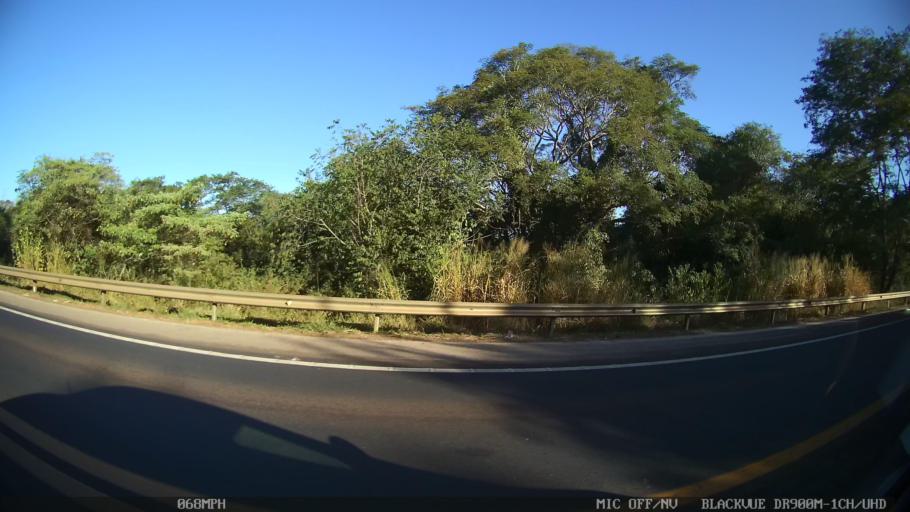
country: BR
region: Sao Paulo
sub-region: Guapiacu
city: Guapiacu
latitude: -20.7434
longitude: -49.1065
